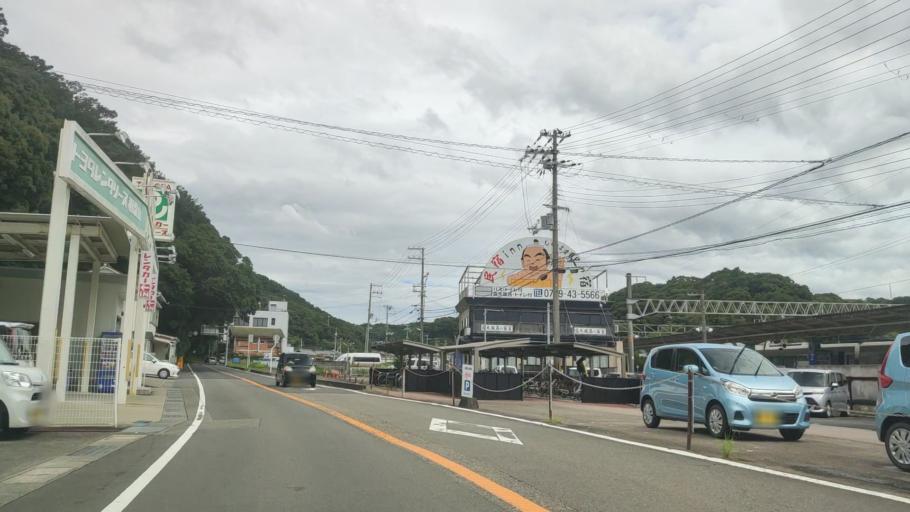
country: JP
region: Wakayama
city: Tanabe
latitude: 33.6762
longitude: 135.3871
